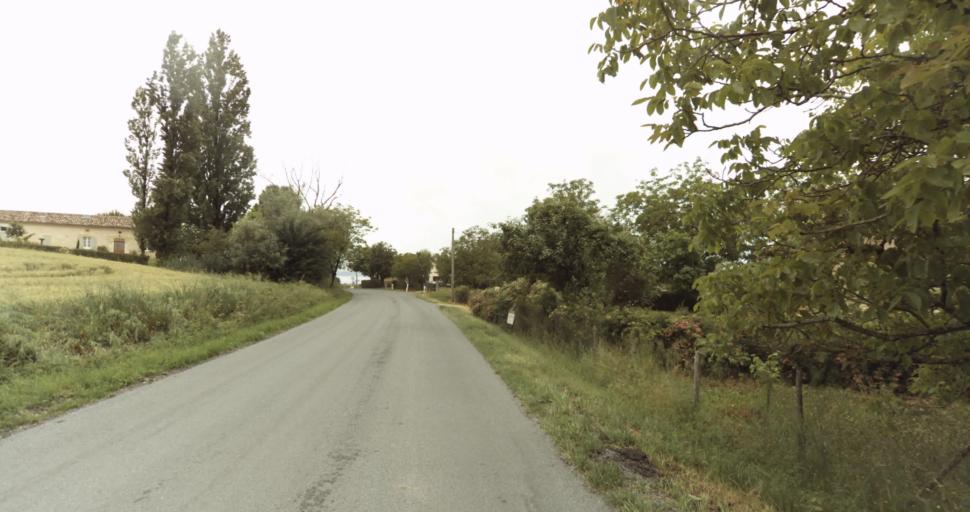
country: FR
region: Aquitaine
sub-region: Departement de la Dordogne
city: Beaumont-du-Perigord
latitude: 44.7060
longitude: 0.8316
